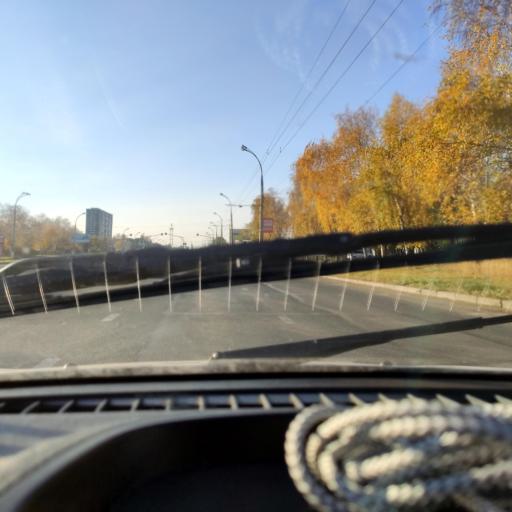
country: RU
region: Samara
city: Tol'yatti
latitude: 53.5442
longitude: 49.2647
